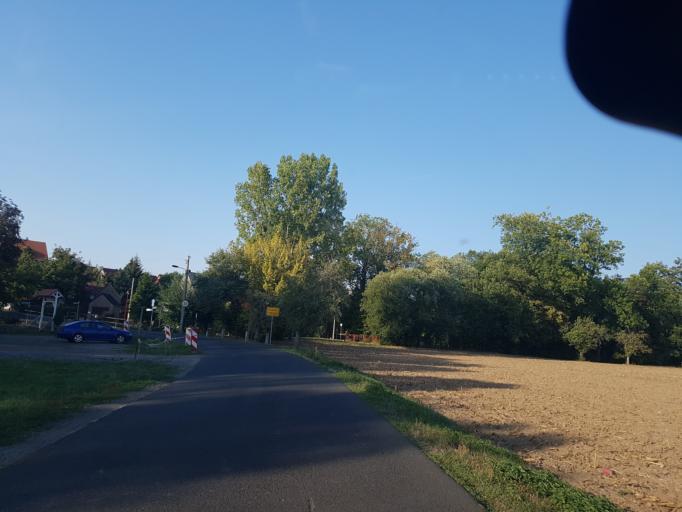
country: DE
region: Saxony
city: Stauchitz
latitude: 51.2603
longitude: 13.2284
